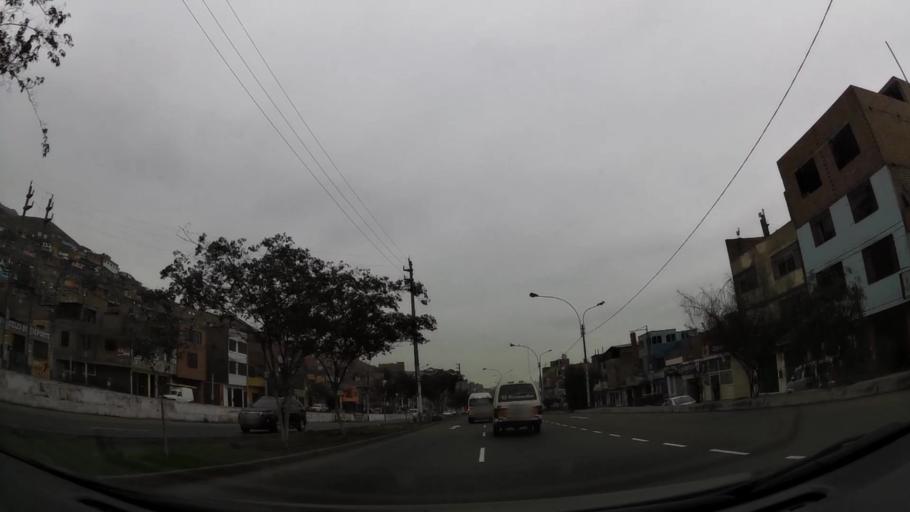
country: PE
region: Lima
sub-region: Lima
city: Independencia
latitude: -11.9608
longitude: -77.0542
